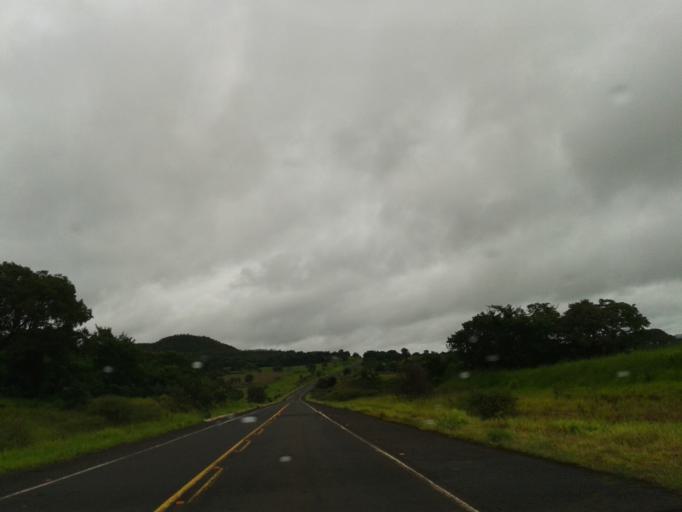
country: BR
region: Minas Gerais
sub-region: Santa Vitoria
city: Santa Vitoria
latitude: -19.2017
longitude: -50.0276
